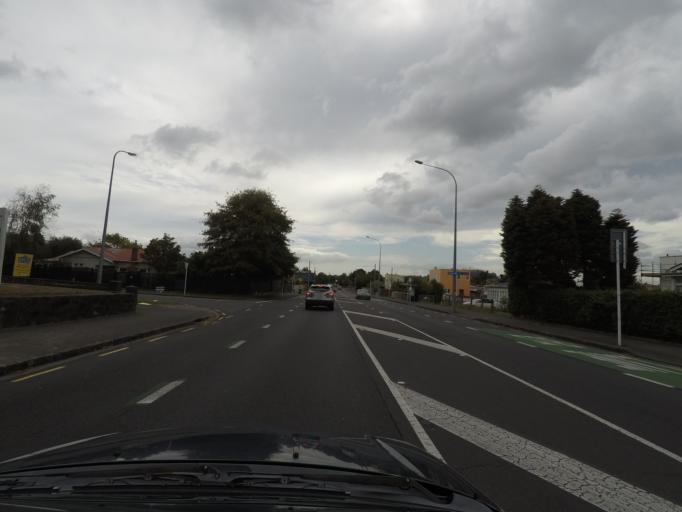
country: NZ
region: Auckland
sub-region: Auckland
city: Auckland
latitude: -36.8945
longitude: 174.7354
